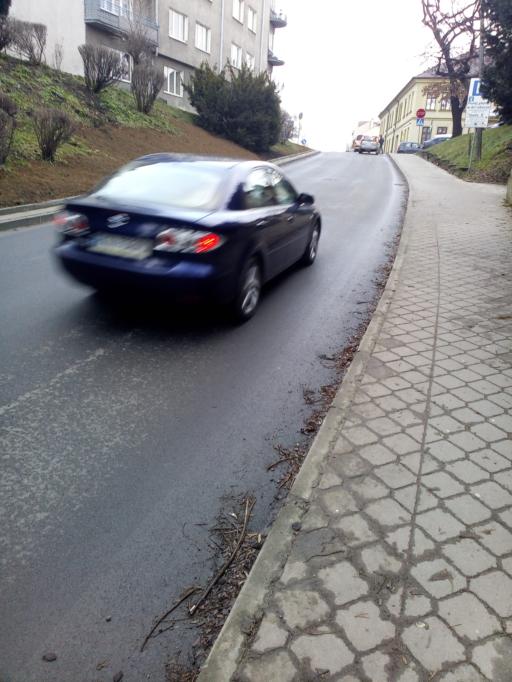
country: PL
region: Lesser Poland Voivodeship
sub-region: Powiat nowosadecki
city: Nowy Sacz
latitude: 49.6183
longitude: 20.6937
